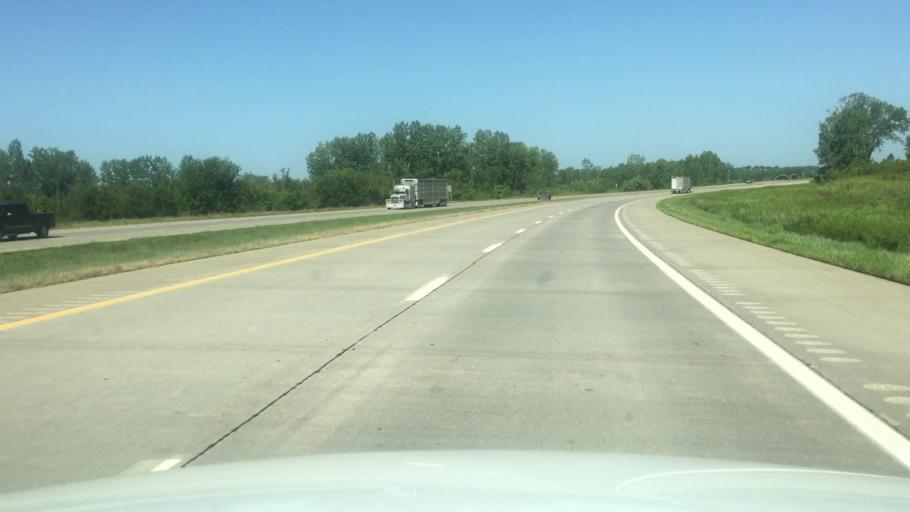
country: US
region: Kansas
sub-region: Doniphan County
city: Wathena
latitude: 39.7412
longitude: -94.9165
